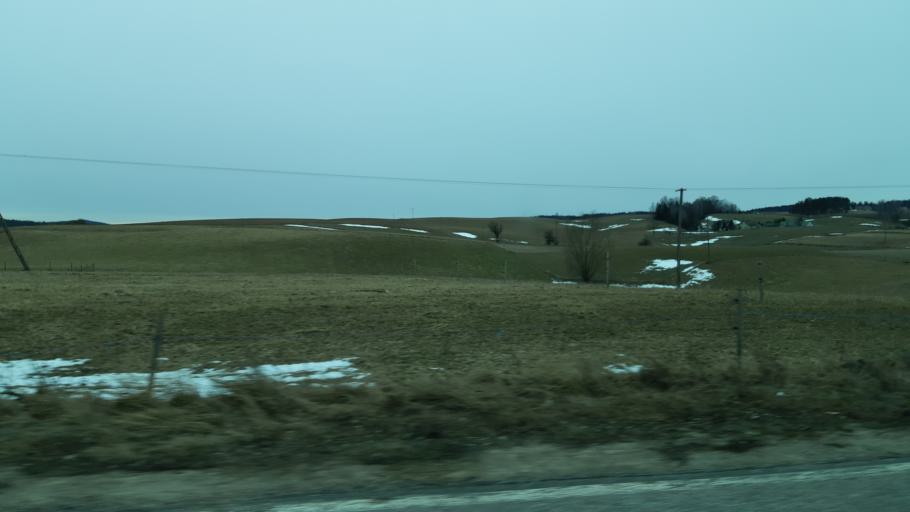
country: PL
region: Podlasie
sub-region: Suwalki
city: Suwalki
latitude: 54.3296
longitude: 22.9570
